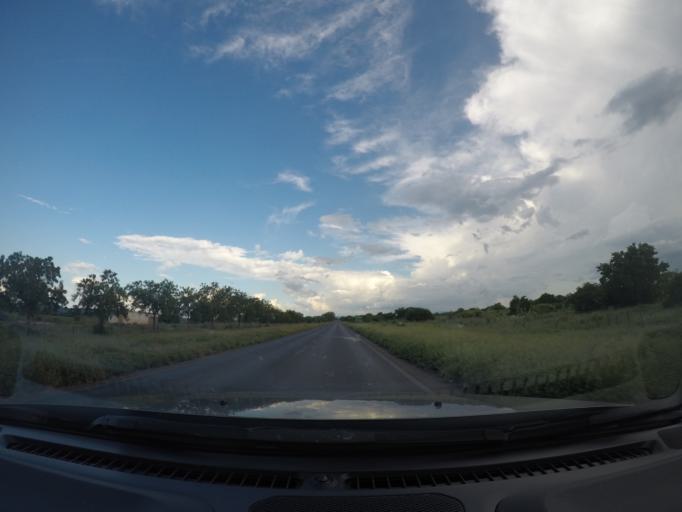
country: BR
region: Bahia
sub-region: Ibotirama
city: Ibotirama
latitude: -12.1387
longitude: -43.3252
